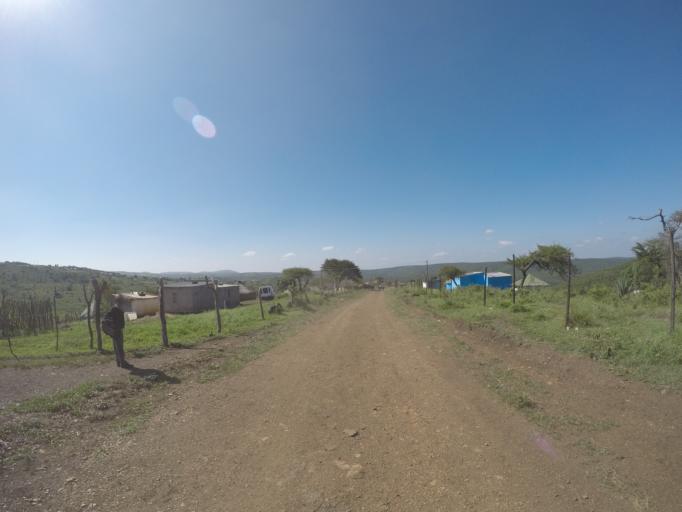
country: ZA
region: KwaZulu-Natal
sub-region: uThungulu District Municipality
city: Empangeni
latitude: -28.5606
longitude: 31.7037
